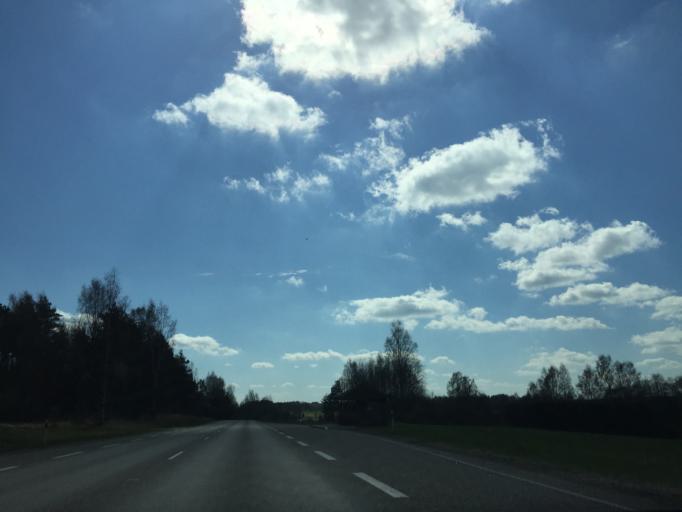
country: EE
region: Tartu
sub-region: Elva linn
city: Elva
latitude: 58.0936
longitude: 26.2264
